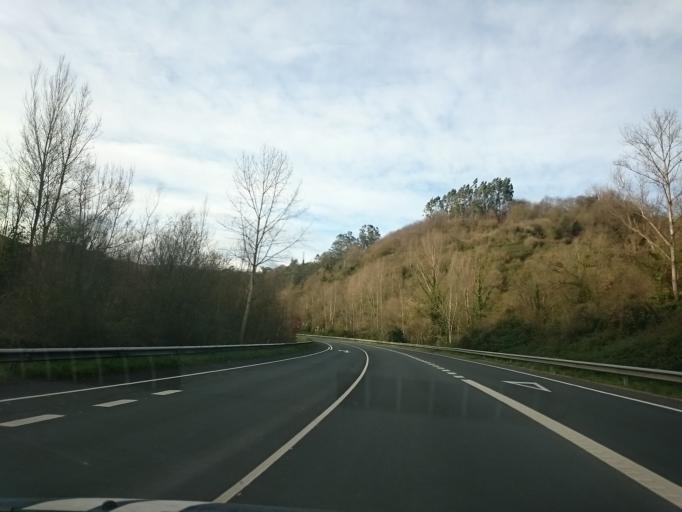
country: ES
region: Asturias
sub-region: Province of Asturias
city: Oviedo
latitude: 43.3113
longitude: -5.8218
